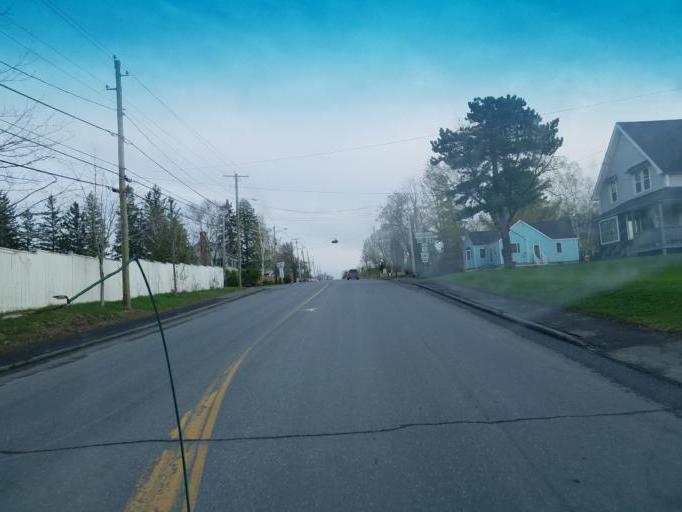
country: US
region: Maine
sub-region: Aroostook County
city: Caribou
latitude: 46.8539
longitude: -68.0111
